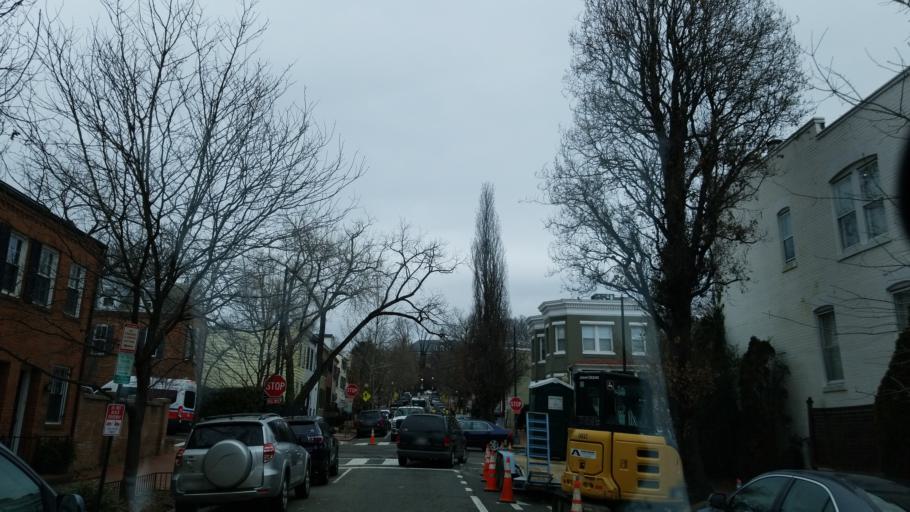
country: US
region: Washington, D.C.
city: Washington, D.C.
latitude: 38.9105
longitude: -77.0661
